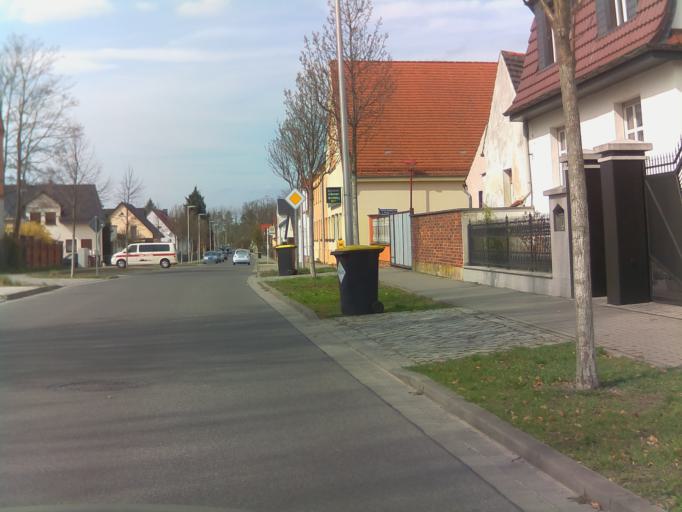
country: DE
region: Brandenburg
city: Cottbus
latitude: 51.7582
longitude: 14.3005
